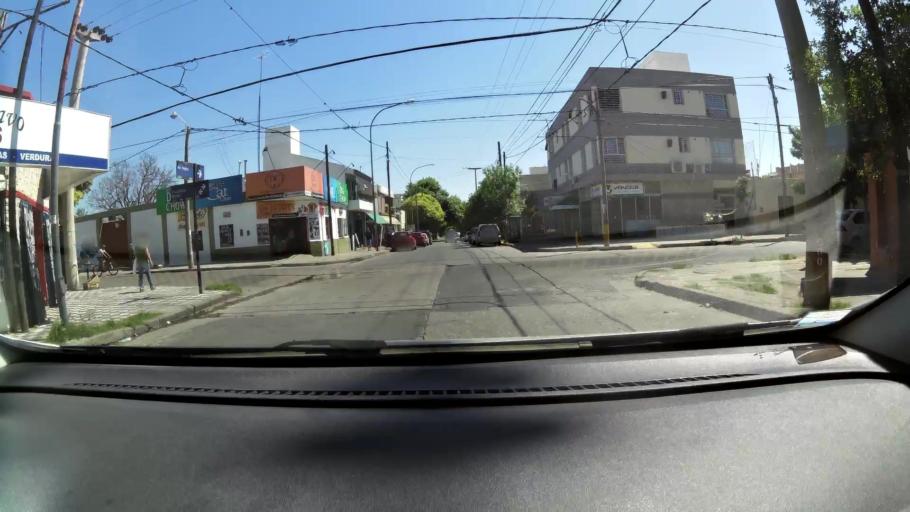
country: AR
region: Cordoba
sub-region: Departamento de Capital
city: Cordoba
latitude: -31.4205
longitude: -64.2086
